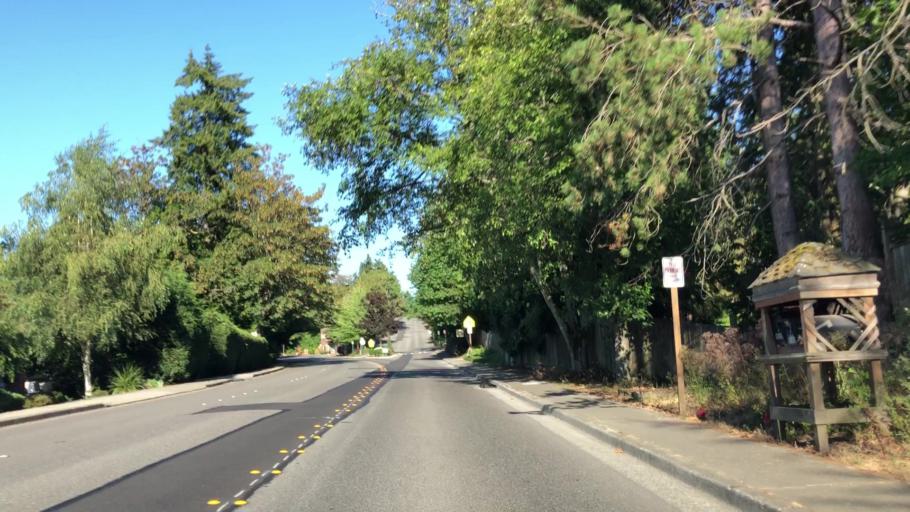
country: US
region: Washington
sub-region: King County
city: Clyde Hill
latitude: 47.6355
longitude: -122.2255
